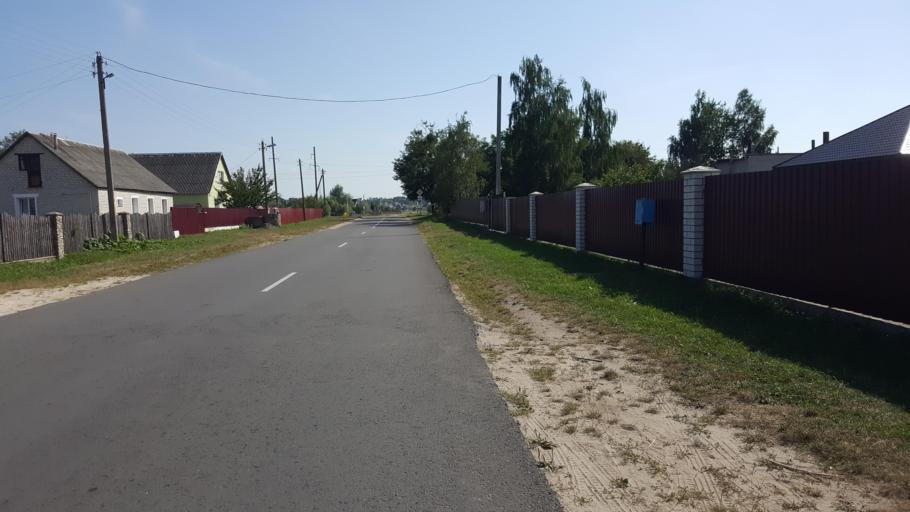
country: BY
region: Brest
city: Kamyanyets
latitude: 52.3958
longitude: 23.8127
